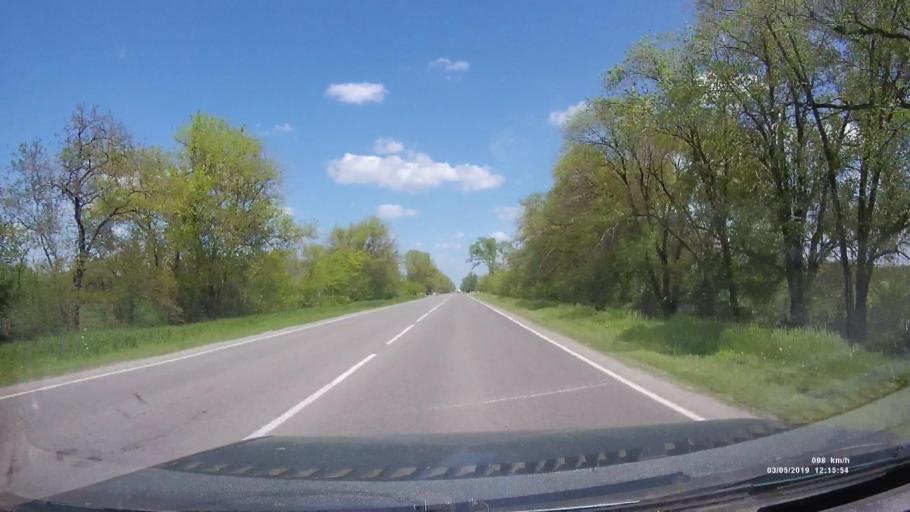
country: RU
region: Rostov
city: Melikhovskaya
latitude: 47.3643
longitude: 40.5786
